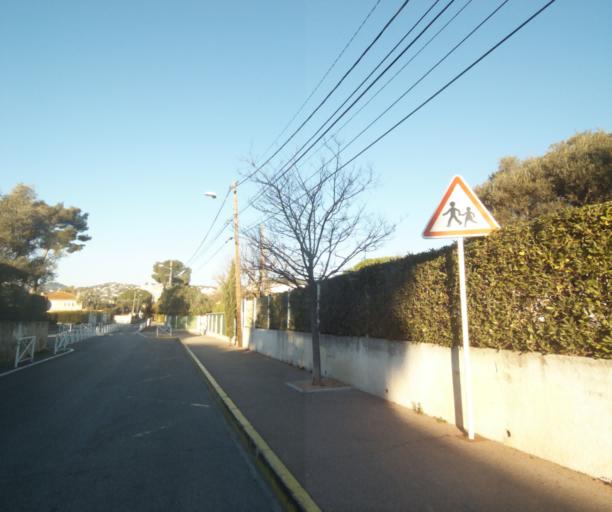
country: FR
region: Provence-Alpes-Cote d'Azur
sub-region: Departement des Alpes-Maritimes
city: Antibes
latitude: 43.5765
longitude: 7.0939
